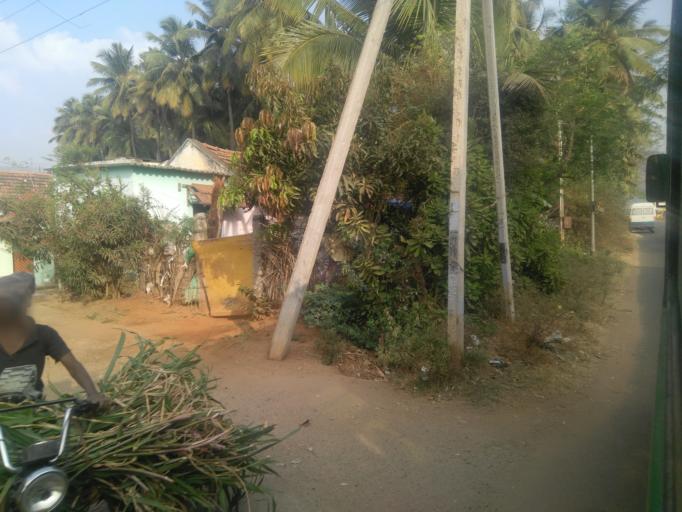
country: IN
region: Tamil Nadu
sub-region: Coimbatore
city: Perur
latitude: 11.0481
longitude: 76.8964
